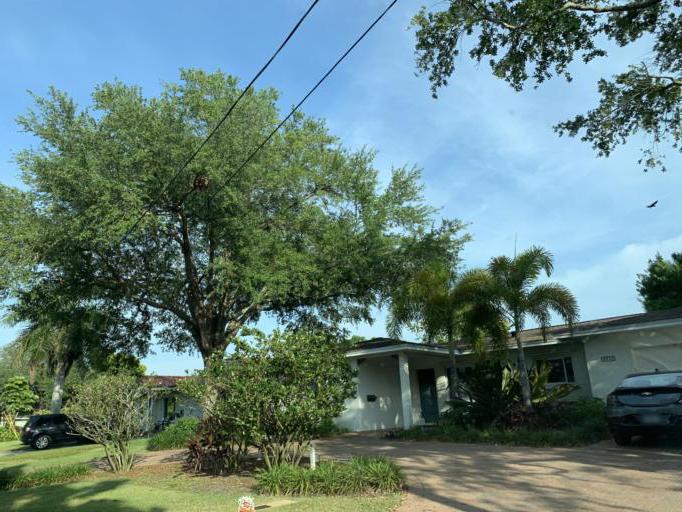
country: US
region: Florida
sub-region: Pinellas County
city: Lealman
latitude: 27.8055
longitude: -82.6213
